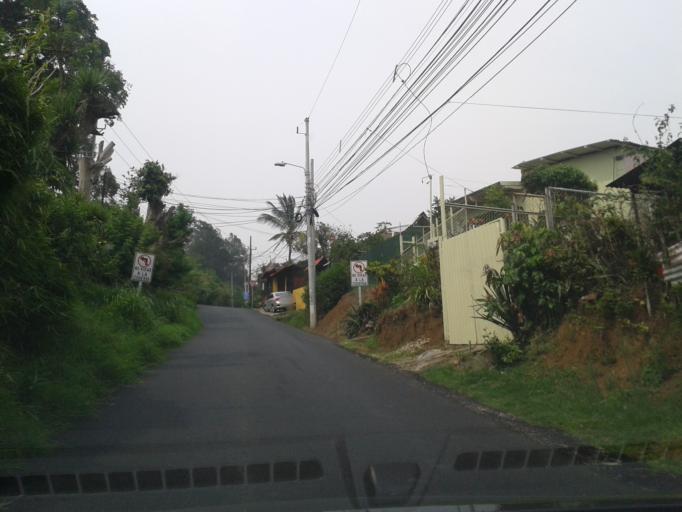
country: CR
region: Heredia
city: San Francisco
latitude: 9.9814
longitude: -84.1344
